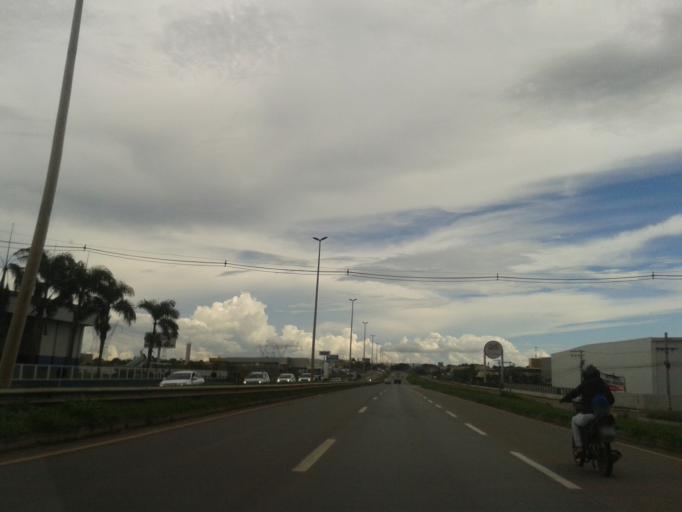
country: BR
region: Goias
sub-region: Aparecida De Goiania
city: Aparecida de Goiania
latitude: -16.8049
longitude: -49.2392
